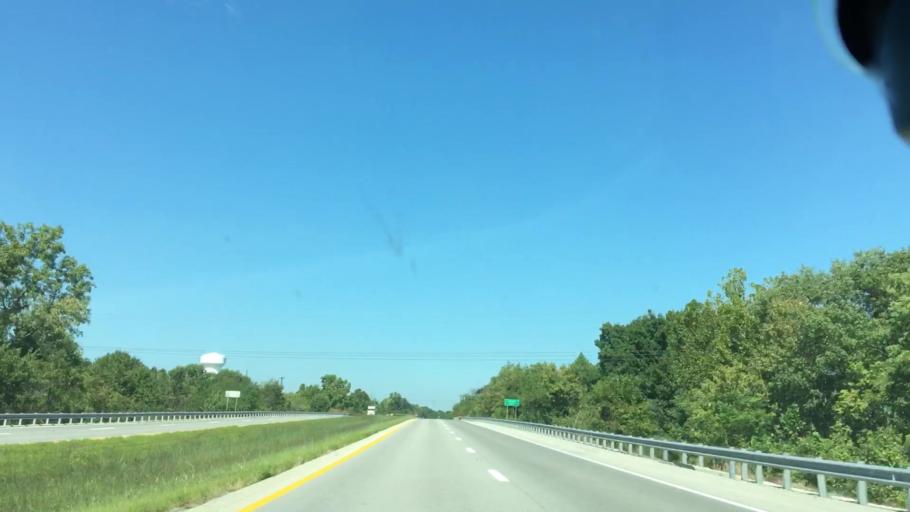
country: US
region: Kentucky
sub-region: Webster County
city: Sebree
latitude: 37.6458
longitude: -87.5113
